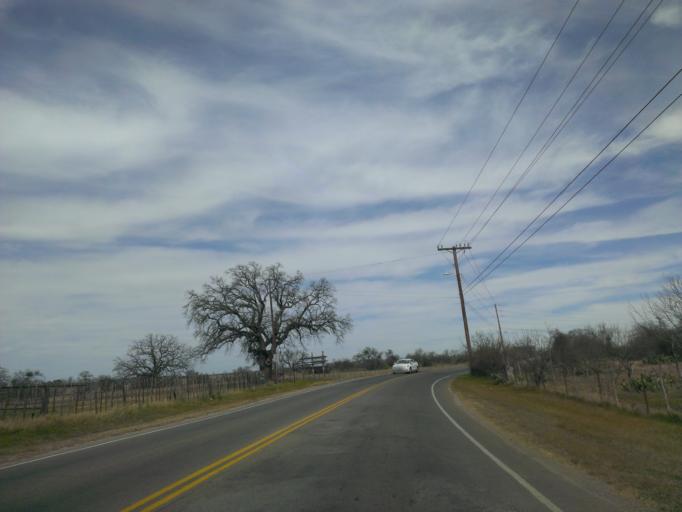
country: US
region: Texas
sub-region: Burnet County
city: Granite Shoals
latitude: 30.5978
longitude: -98.3810
